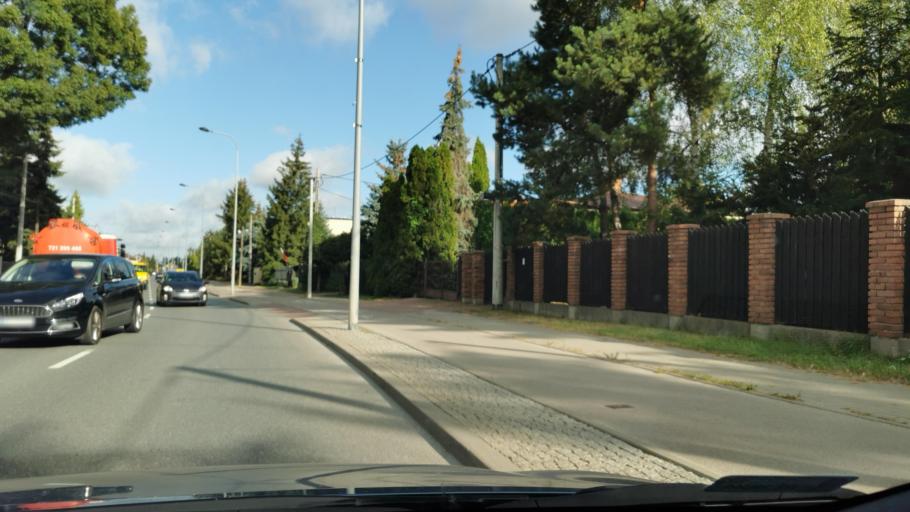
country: PL
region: Masovian Voivodeship
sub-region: Warszawa
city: Kabaty
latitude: 52.1297
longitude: 21.1037
